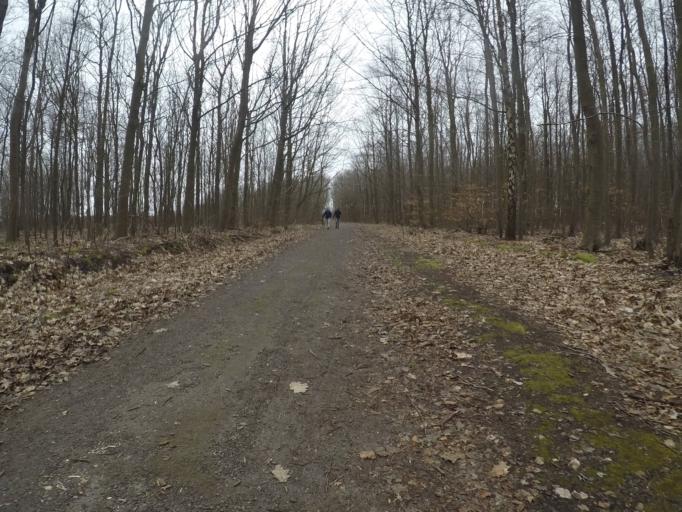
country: DE
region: Lower Saxony
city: Cuxhaven
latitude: 53.8316
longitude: 8.6451
